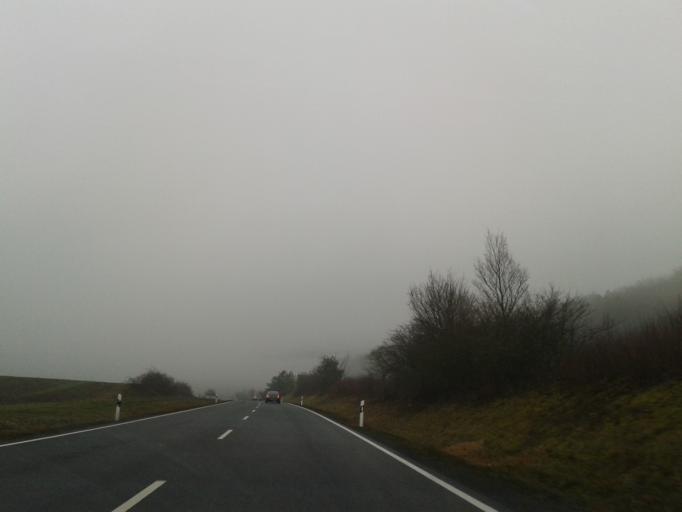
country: DE
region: Bavaria
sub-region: Regierungsbezirk Unterfranken
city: Hofheim in Unterfranken
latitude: 50.1246
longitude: 10.5648
